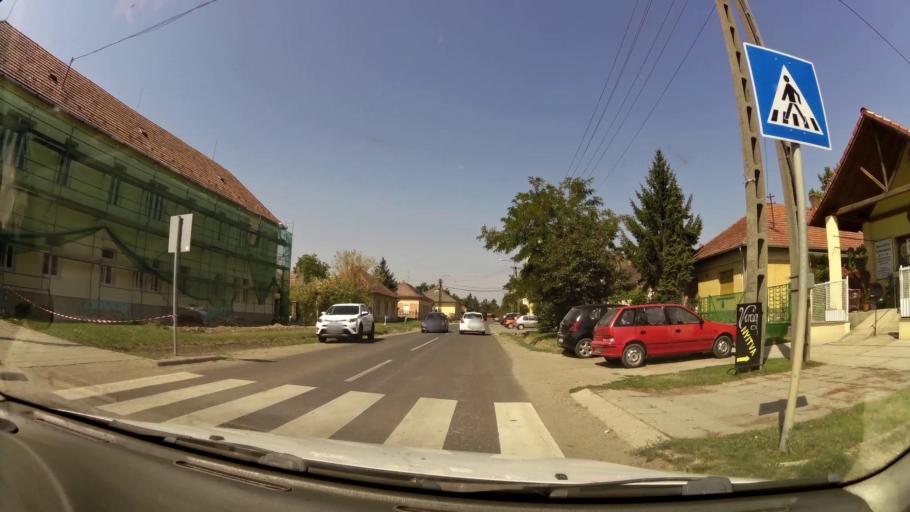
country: HU
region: Pest
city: Tapiobicske
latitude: 47.3610
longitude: 19.6887
